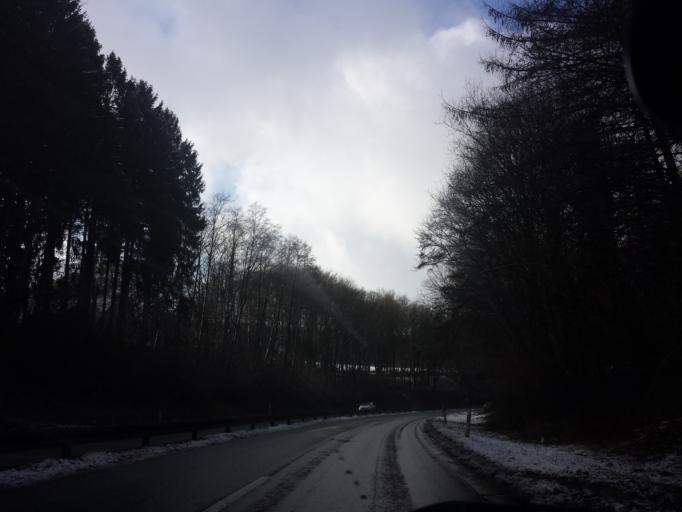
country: DE
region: North Rhine-Westphalia
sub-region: Regierungsbezirk Dusseldorf
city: Solingen
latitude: 51.2293
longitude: 7.0947
